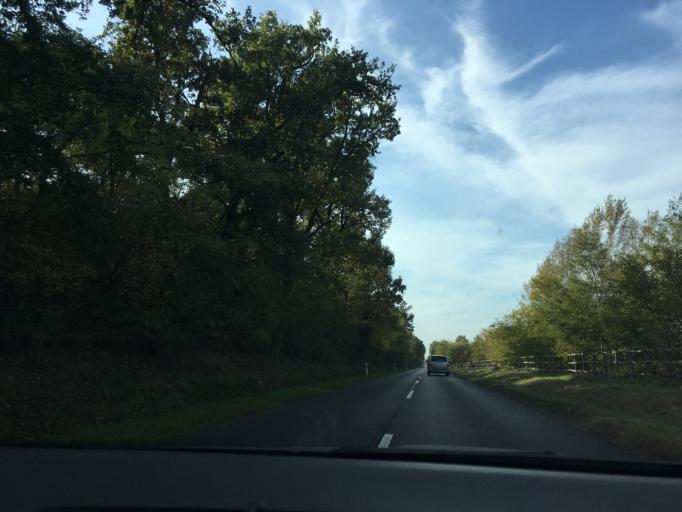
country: HU
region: Hajdu-Bihar
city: Vamospercs
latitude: 47.5276
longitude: 21.8575
